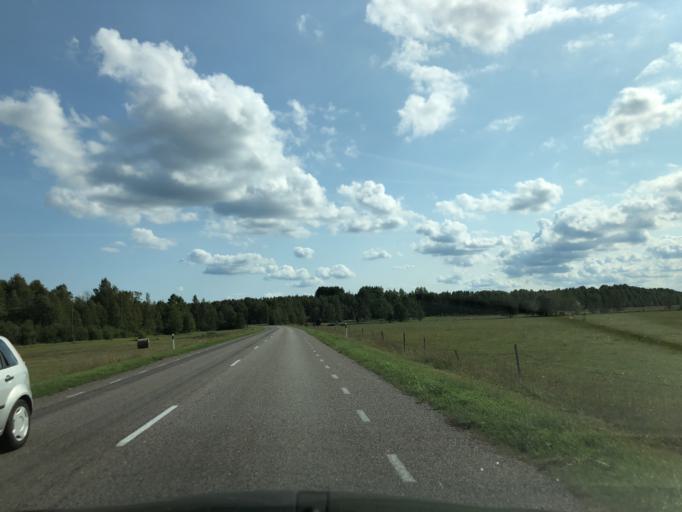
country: EE
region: Hiiumaa
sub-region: Kaerdla linn
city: Kardla
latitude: 58.7223
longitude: 22.5626
